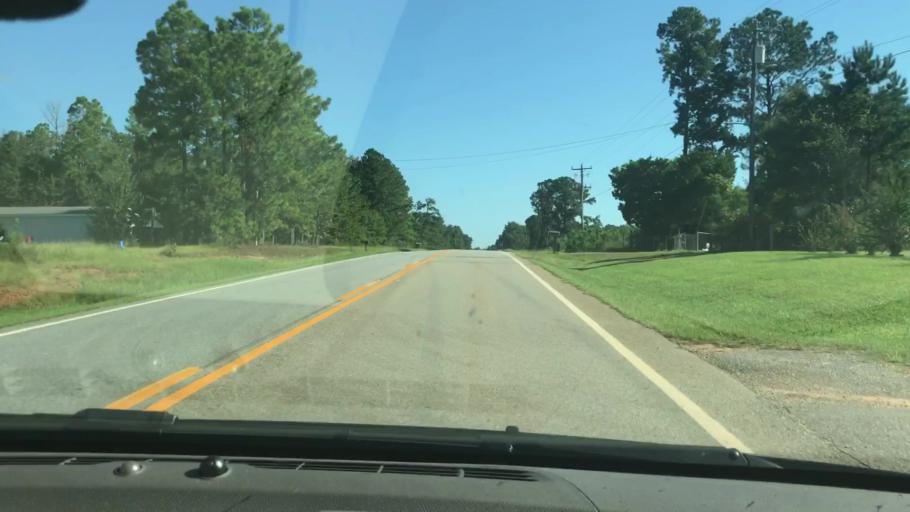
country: US
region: Georgia
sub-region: Quitman County
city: Georgetown
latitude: 31.8507
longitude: -85.0727
